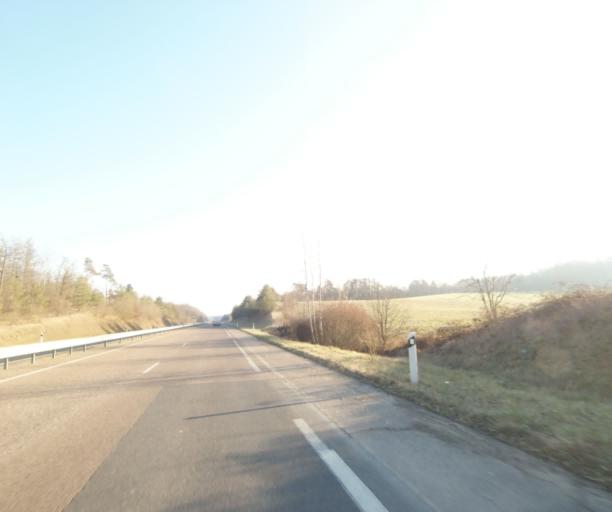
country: FR
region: Champagne-Ardenne
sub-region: Departement de la Haute-Marne
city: Chevillon
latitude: 48.5079
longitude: 5.0974
